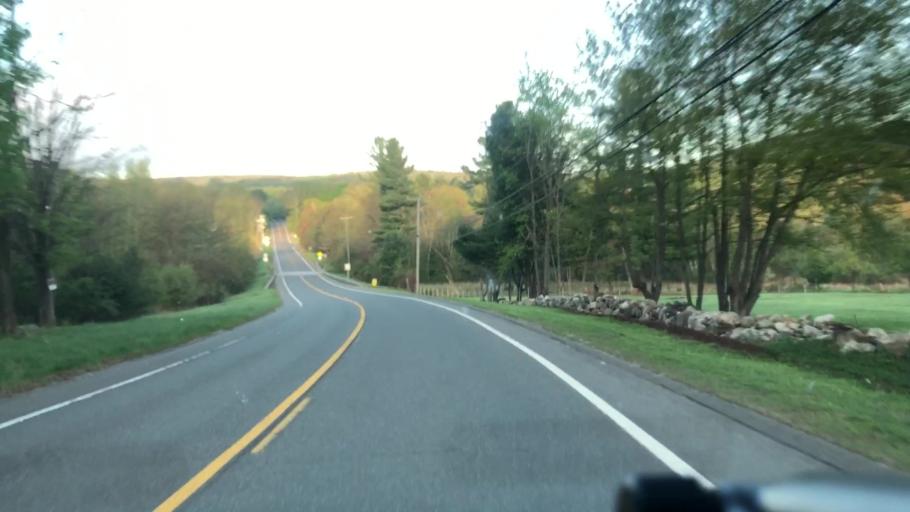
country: US
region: Massachusetts
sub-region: Hampshire County
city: Westhampton
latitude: 42.2867
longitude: -72.7704
